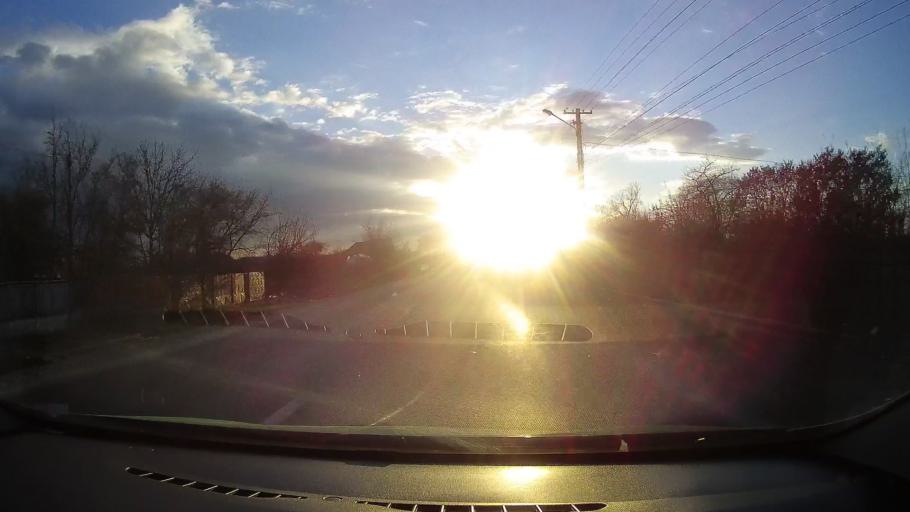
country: RO
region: Dambovita
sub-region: Comuna Gura Ocnitei
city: Adanca
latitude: 44.9082
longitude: 25.6274
